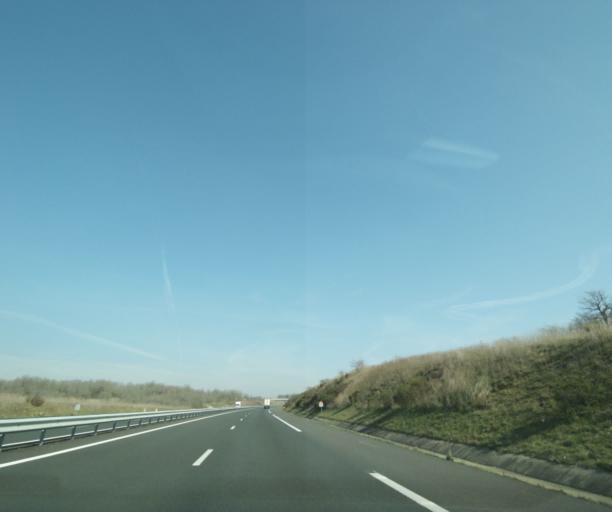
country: FR
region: Midi-Pyrenees
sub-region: Departement du Lot
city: Pradines
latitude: 44.5691
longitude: 1.5123
